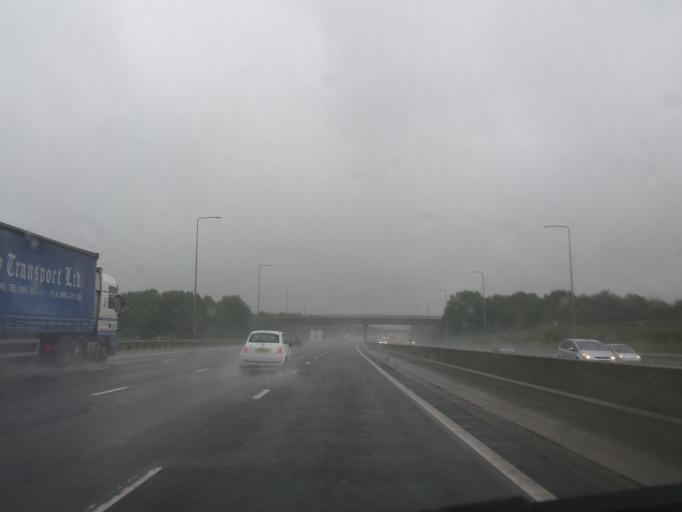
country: GB
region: England
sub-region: Nottinghamshire
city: Hucknall
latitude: 53.0325
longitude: -1.2485
